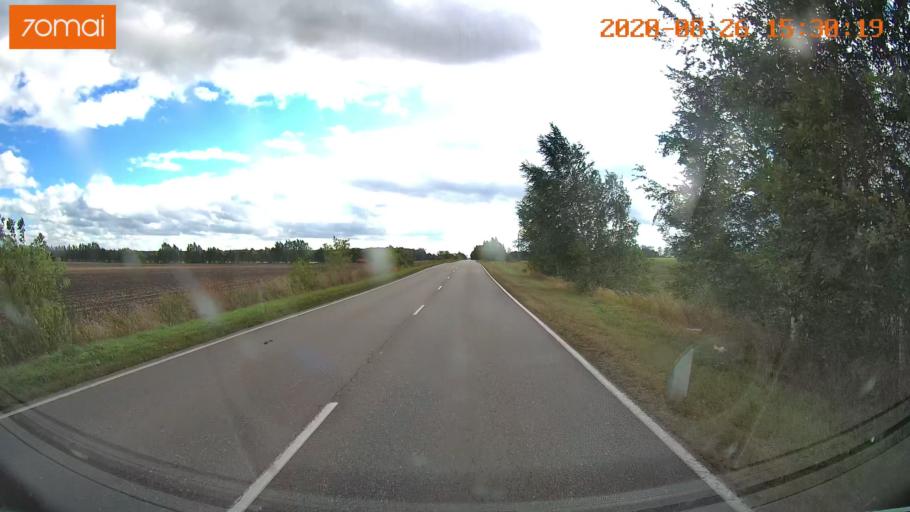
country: RU
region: Tula
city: Severo-Zadonsk
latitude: 54.0928
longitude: 38.3984
